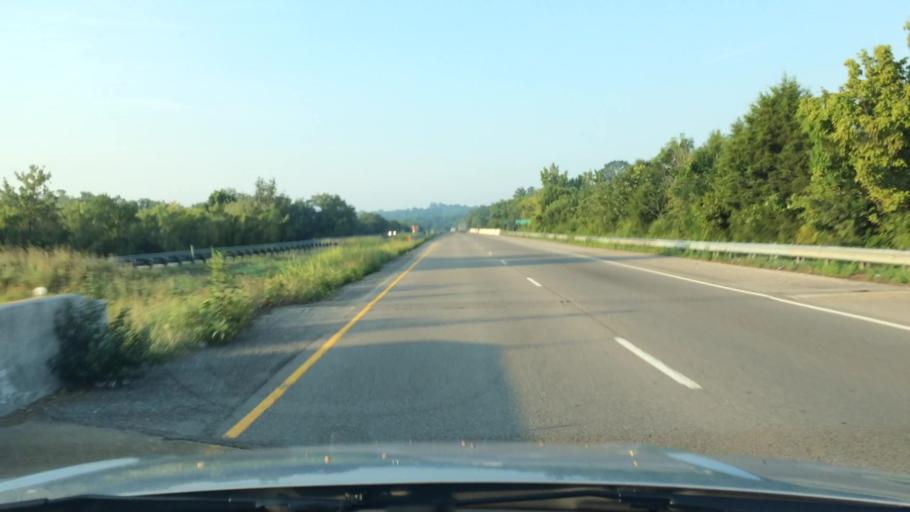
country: US
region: Tennessee
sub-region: Giles County
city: Pulaski
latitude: 35.1979
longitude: -87.0638
